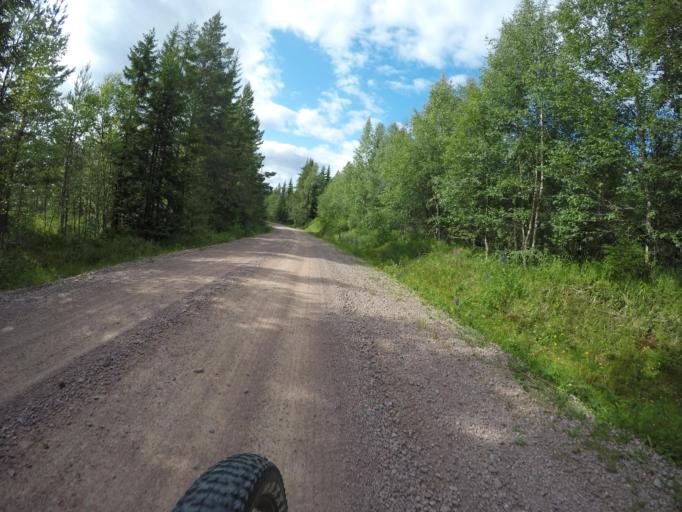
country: SE
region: Vaermland
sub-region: Filipstads Kommun
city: Lesjofors
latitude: 60.1120
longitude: 14.4782
